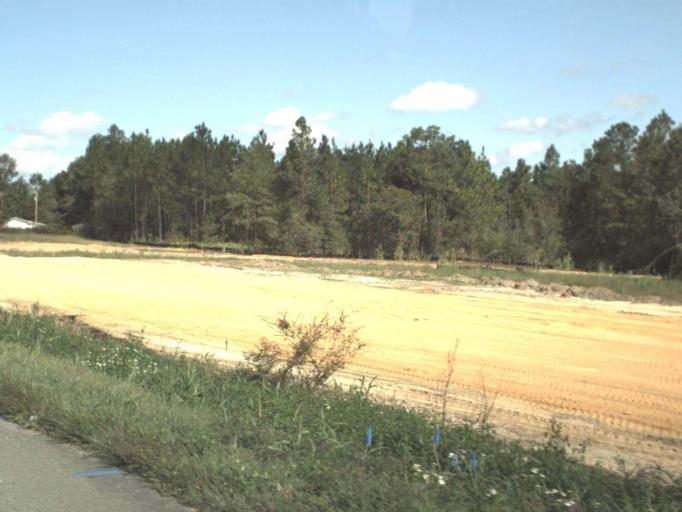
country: US
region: Florida
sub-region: Walton County
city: DeFuniak Springs
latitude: 30.6539
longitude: -86.1159
